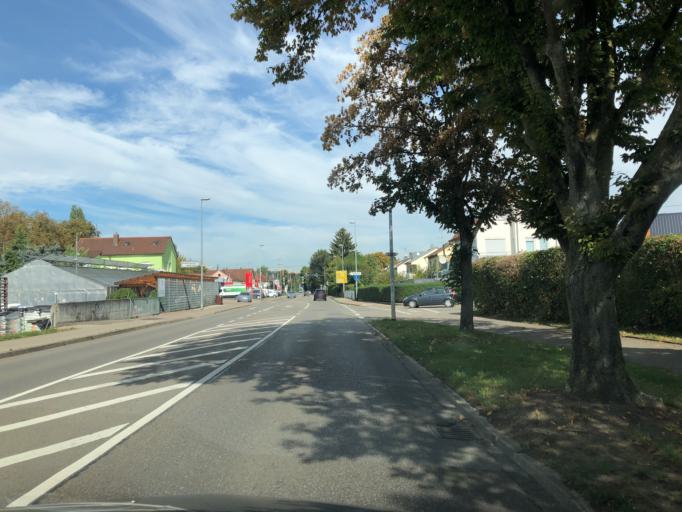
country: DE
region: Baden-Wuerttemberg
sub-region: Regierungsbezirk Stuttgart
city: Nurtingen
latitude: 48.6136
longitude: 9.3485
